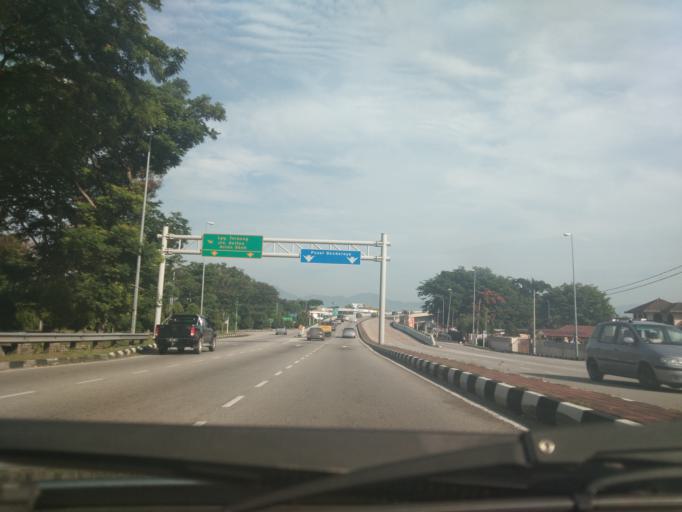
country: MY
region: Perak
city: Ipoh
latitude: 4.5765
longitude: 101.1087
